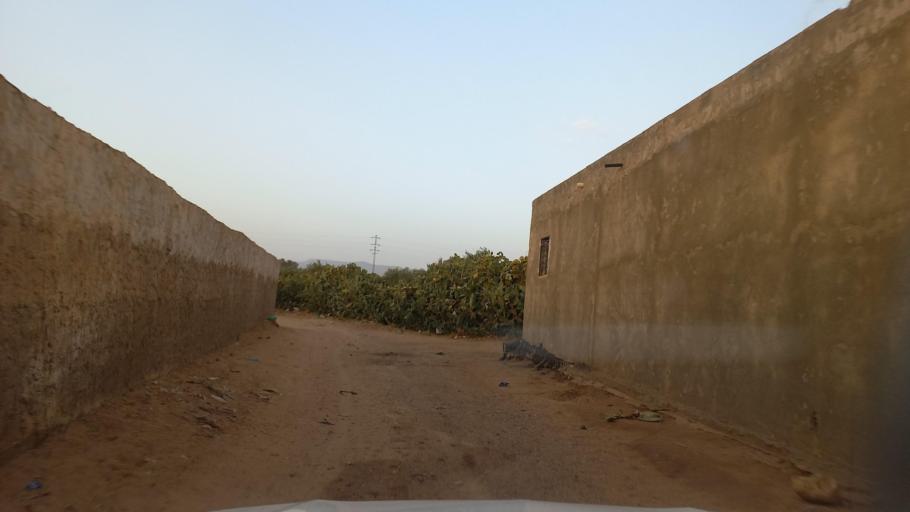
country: TN
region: Al Qasrayn
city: Kasserine
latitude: 35.2678
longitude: 9.0580
